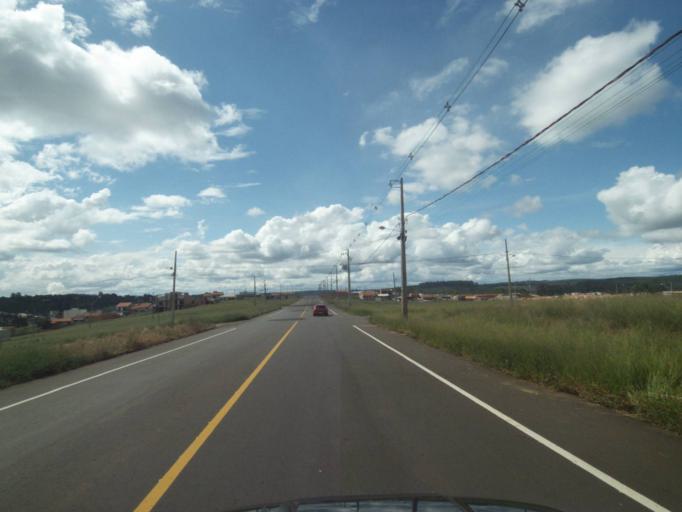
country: BR
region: Parana
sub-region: Telemaco Borba
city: Telemaco Borba
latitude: -24.3136
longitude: -50.6377
